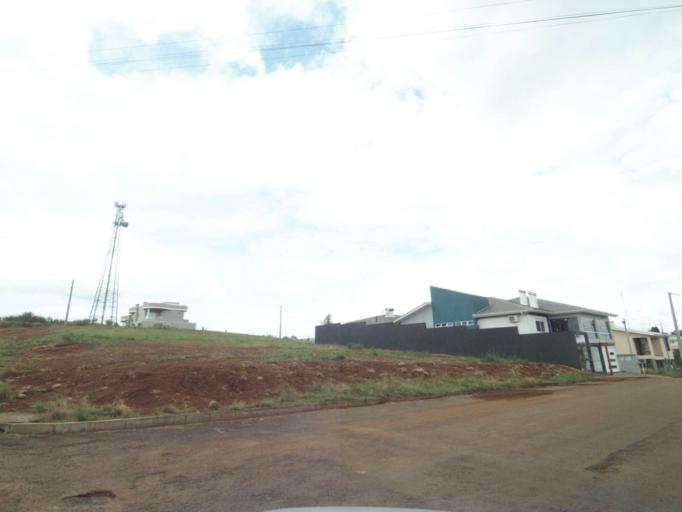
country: BR
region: Rio Grande do Sul
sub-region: Lagoa Vermelha
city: Lagoa Vermelha
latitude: -28.2204
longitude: -51.5174
